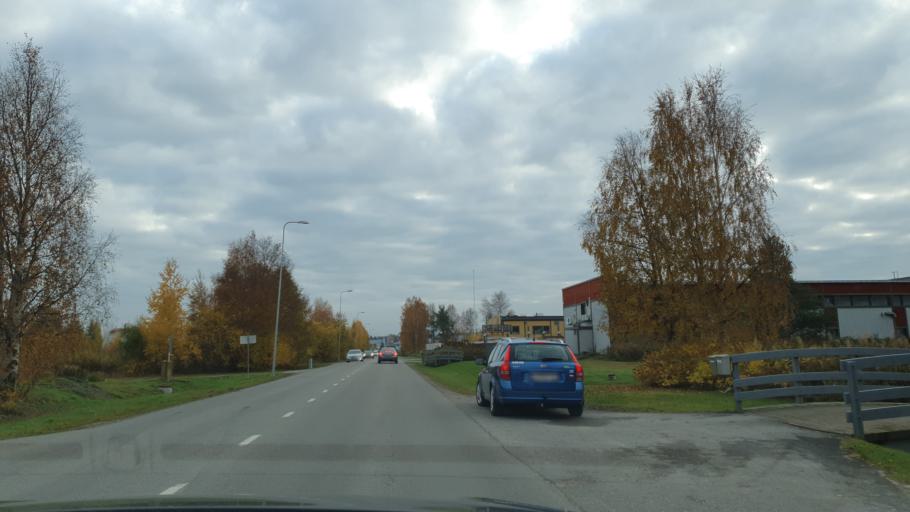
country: FI
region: Lapland
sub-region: Rovaniemi
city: Rovaniemi
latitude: 66.4943
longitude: 25.6742
